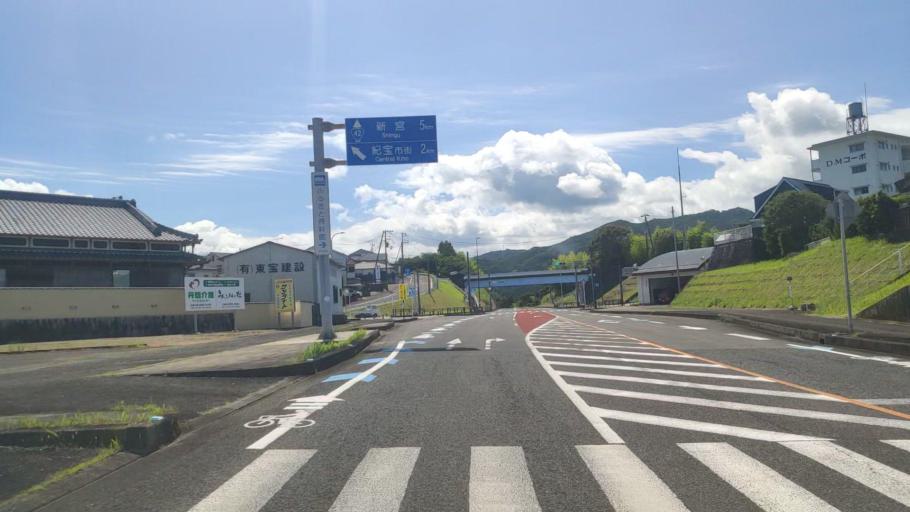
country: JP
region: Wakayama
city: Shingu
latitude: 33.7456
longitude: 136.0156
